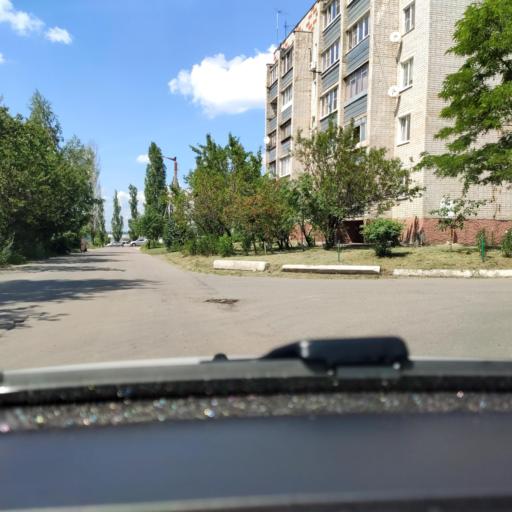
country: RU
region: Voronezj
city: Semiluki
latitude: 51.6950
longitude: 39.0092
